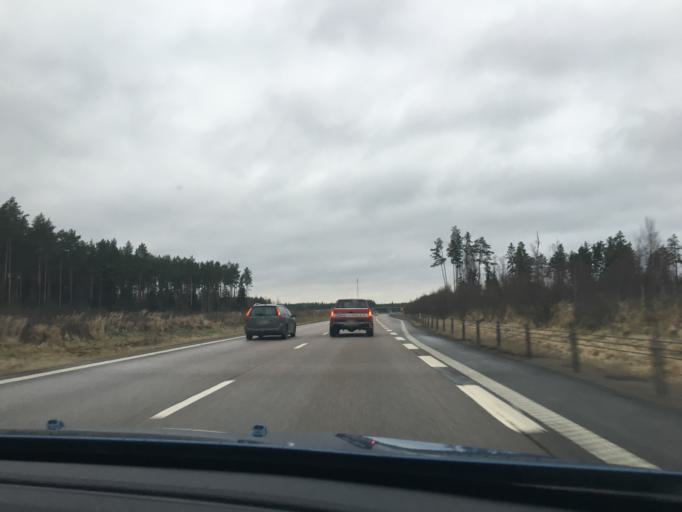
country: SE
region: Uppsala
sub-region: Tierps Kommun
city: Tierp
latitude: 60.4338
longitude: 17.4258
